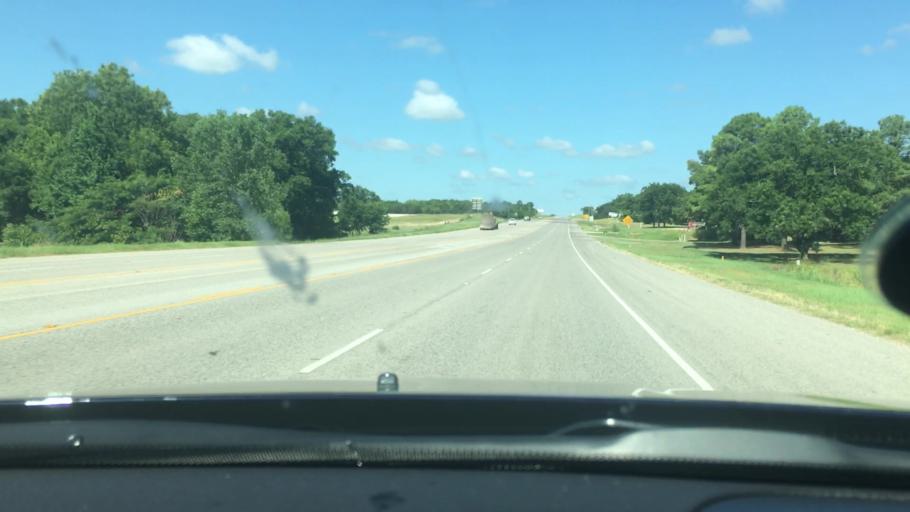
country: US
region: Oklahoma
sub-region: Marshall County
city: Oakland
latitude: 34.1001
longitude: -96.8047
